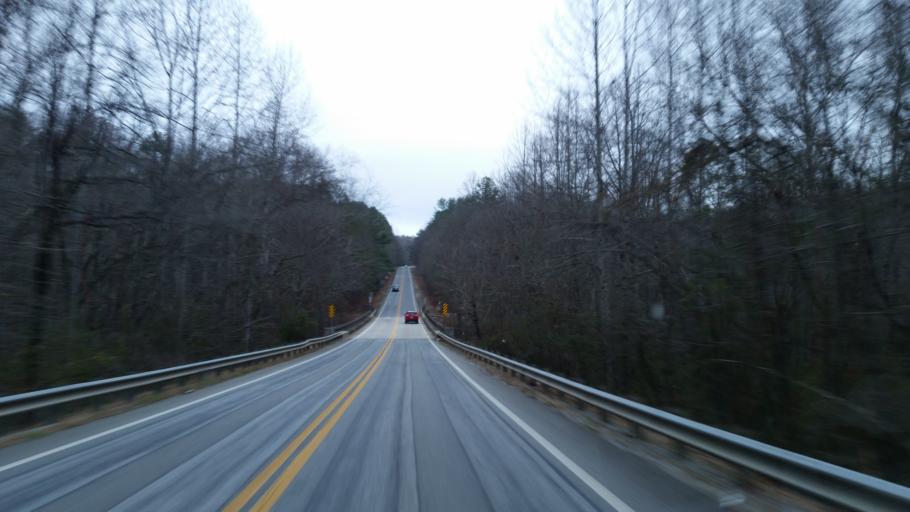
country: US
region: Georgia
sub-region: Dawson County
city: Dawsonville
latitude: 34.4098
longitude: -84.0207
